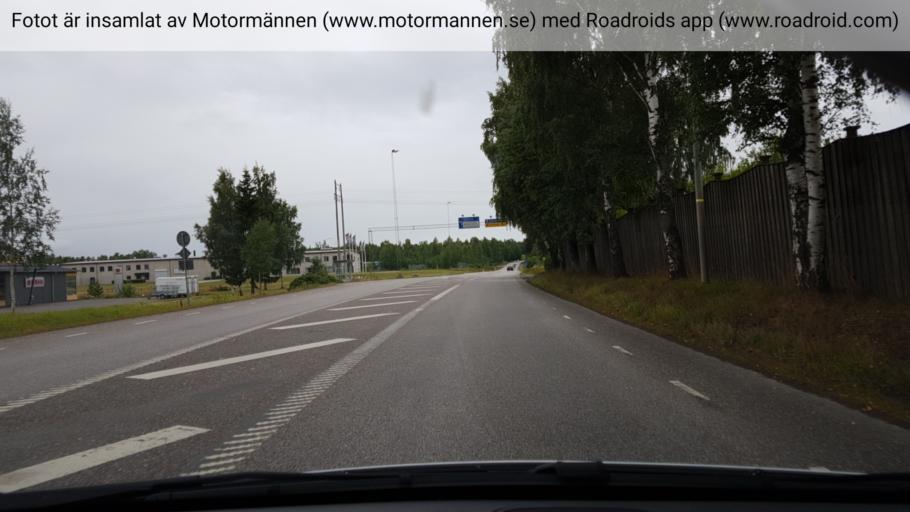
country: SE
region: Vaestra Goetaland
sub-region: Tibro Kommun
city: Tibro
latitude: 58.4215
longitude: 14.1316
